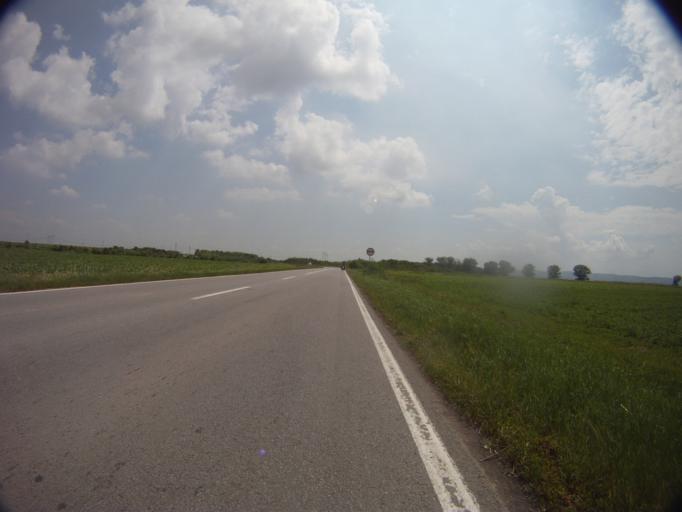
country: RS
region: Autonomna Pokrajina Vojvodina
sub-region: Juznobanatski Okrug
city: Pancevo
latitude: 44.7936
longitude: 20.7203
